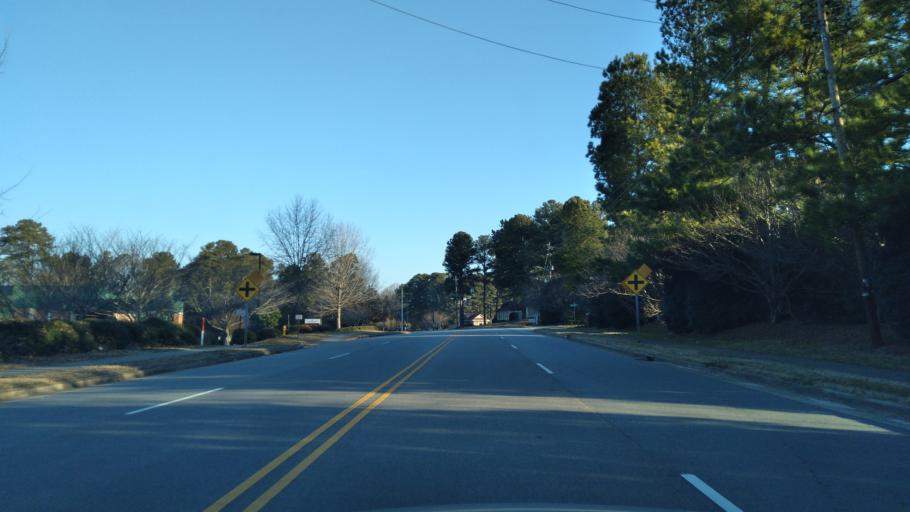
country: US
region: North Carolina
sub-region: Wake County
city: Garner
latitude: 35.6958
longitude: -78.6165
